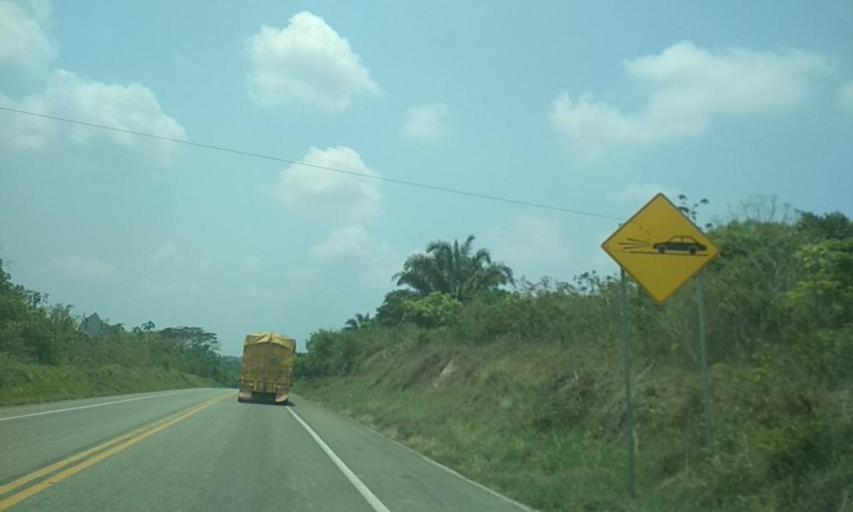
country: MX
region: Tabasco
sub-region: Huimanguillo
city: Francisco Rueda
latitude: 17.7323
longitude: -93.9700
